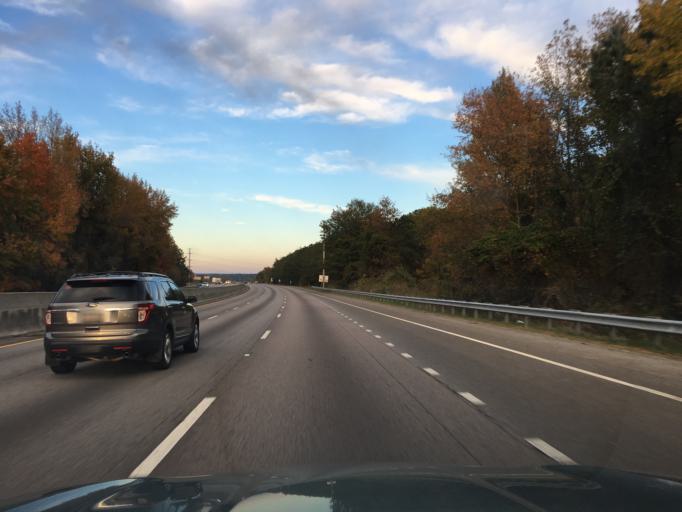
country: US
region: South Carolina
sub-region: Lexington County
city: Saint Andrews
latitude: 34.0144
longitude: -81.1417
